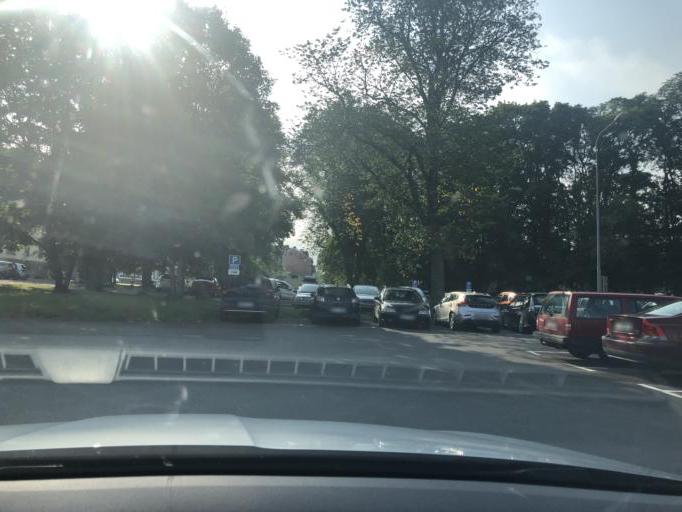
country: SE
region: Joenkoeping
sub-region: Eksjo Kommun
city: Eksjoe
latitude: 57.6674
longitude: 14.9684
